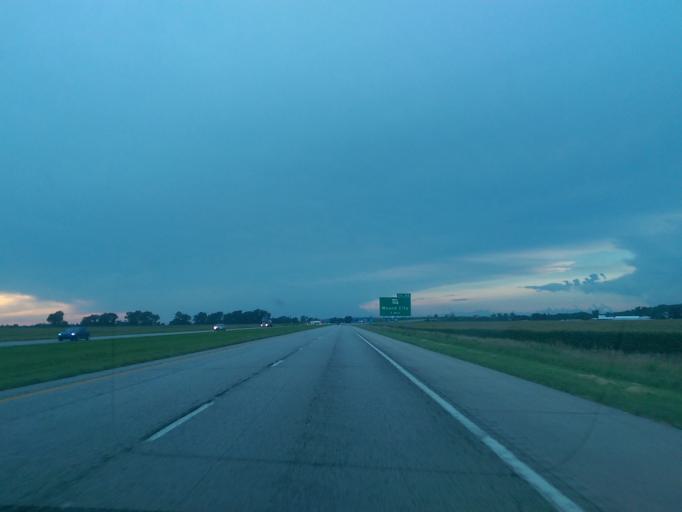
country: US
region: Missouri
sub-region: Holt County
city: Mound City
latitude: 40.1176
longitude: -95.2271
